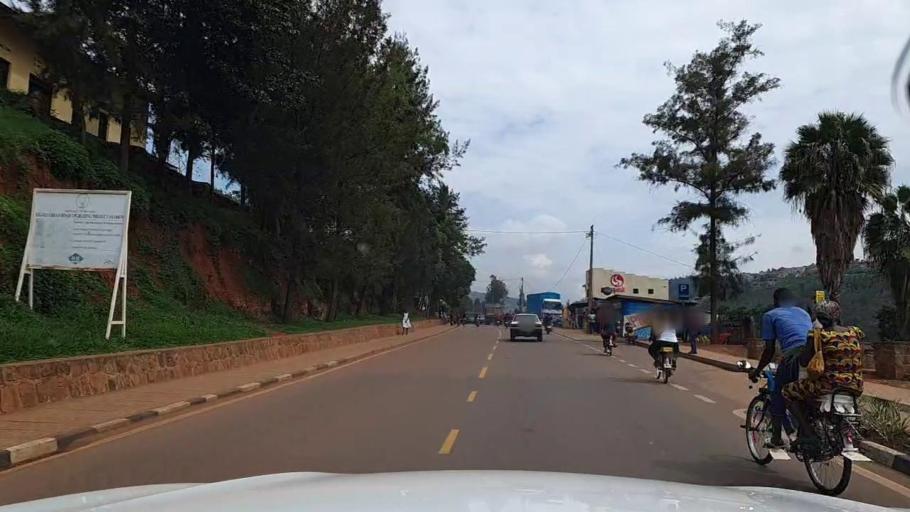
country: RW
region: Kigali
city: Kigali
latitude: -1.9325
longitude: 30.0455
